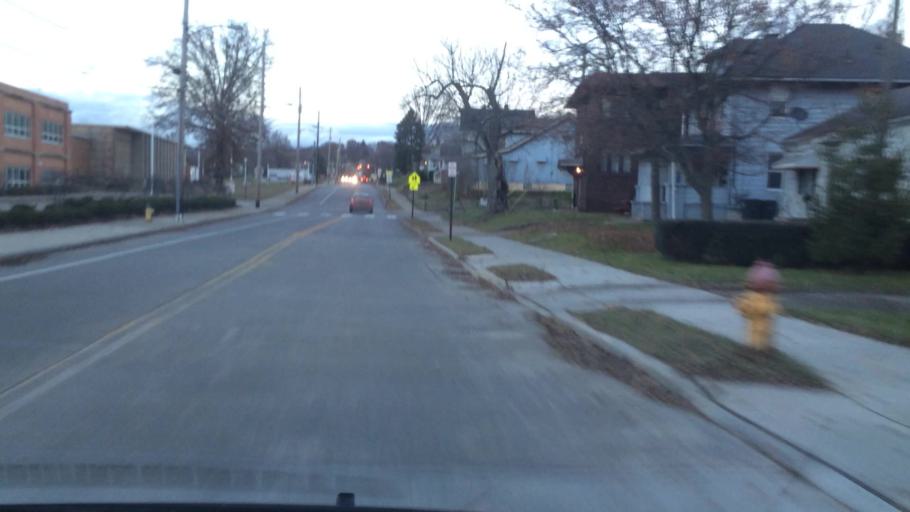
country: US
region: Ohio
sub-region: Summit County
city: Sawyerwood
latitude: 41.0631
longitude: -81.4667
